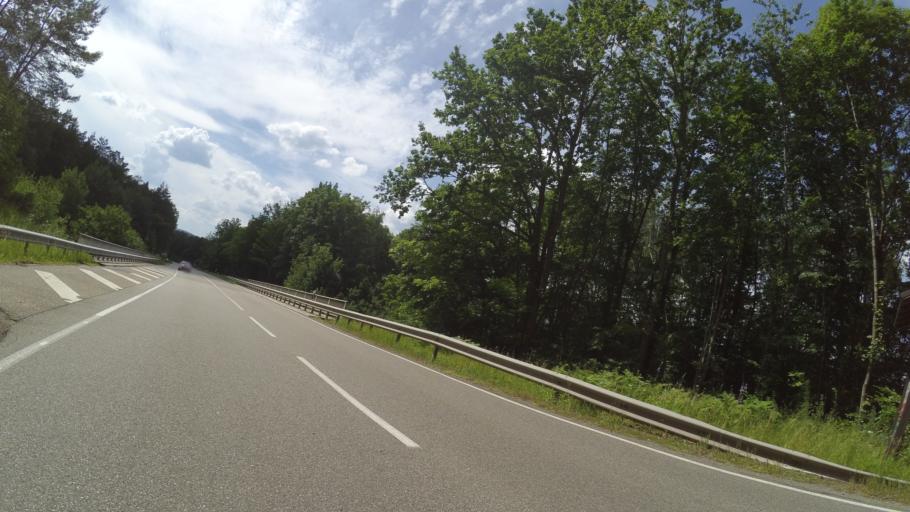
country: DE
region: Rheinland-Pfalz
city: Landstuhl
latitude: 49.4044
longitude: 7.5820
